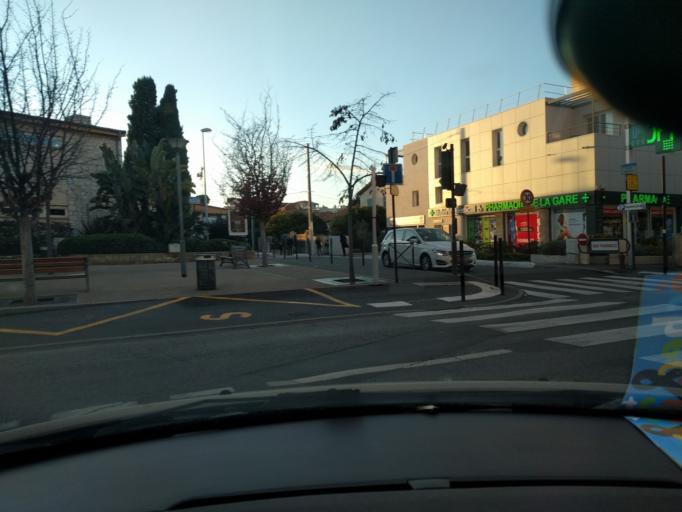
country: FR
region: Provence-Alpes-Cote d'Azur
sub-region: Departement des Alpes-Maritimes
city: Saint-Laurent-du-Var
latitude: 43.6643
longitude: 7.1937
